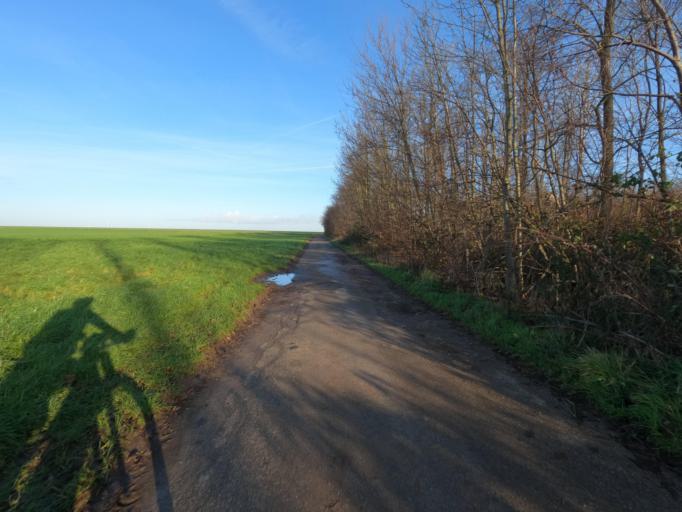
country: DE
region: North Rhine-Westphalia
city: Julich
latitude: 50.9292
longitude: 6.3986
